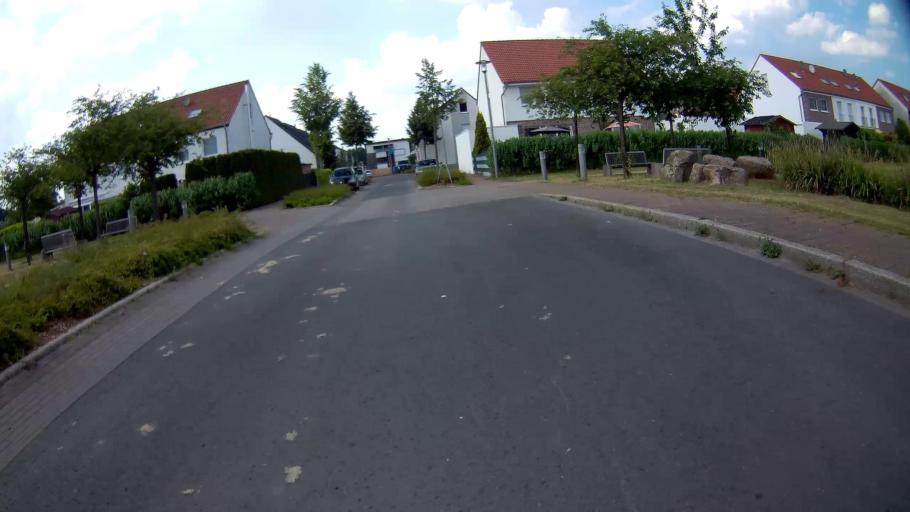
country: DE
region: North Rhine-Westphalia
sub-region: Regierungsbezirk Munster
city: Gladbeck
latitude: 51.5891
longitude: 6.9564
